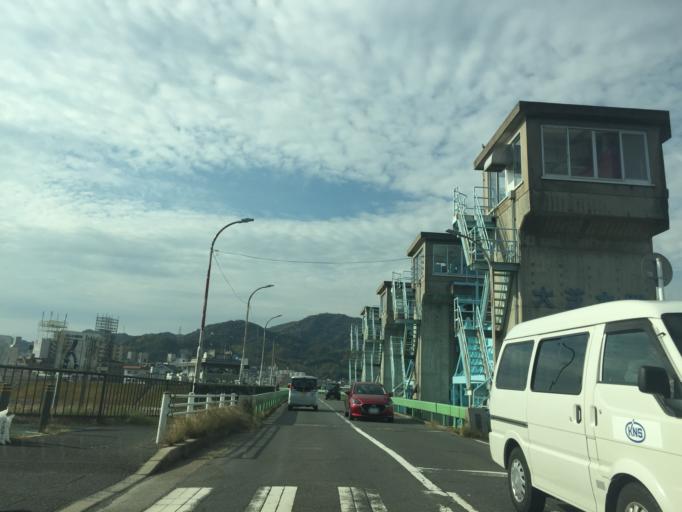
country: JP
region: Hiroshima
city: Hiroshima-shi
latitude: 34.4244
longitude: 132.4648
